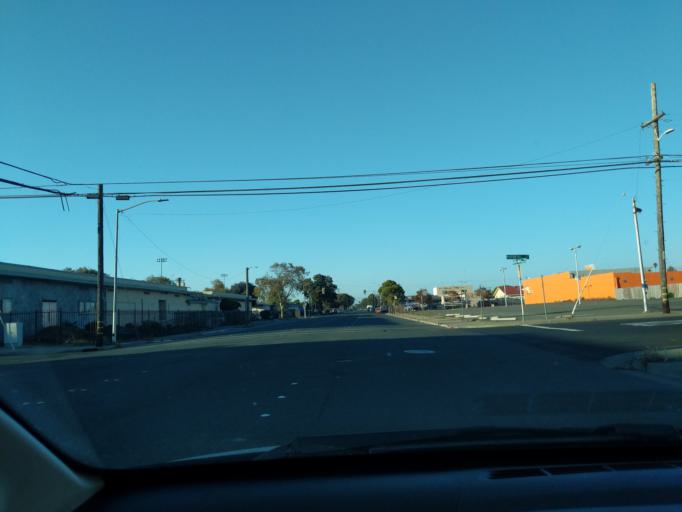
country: US
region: California
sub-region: Contra Costa County
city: Richmond
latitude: 37.9238
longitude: -122.3558
